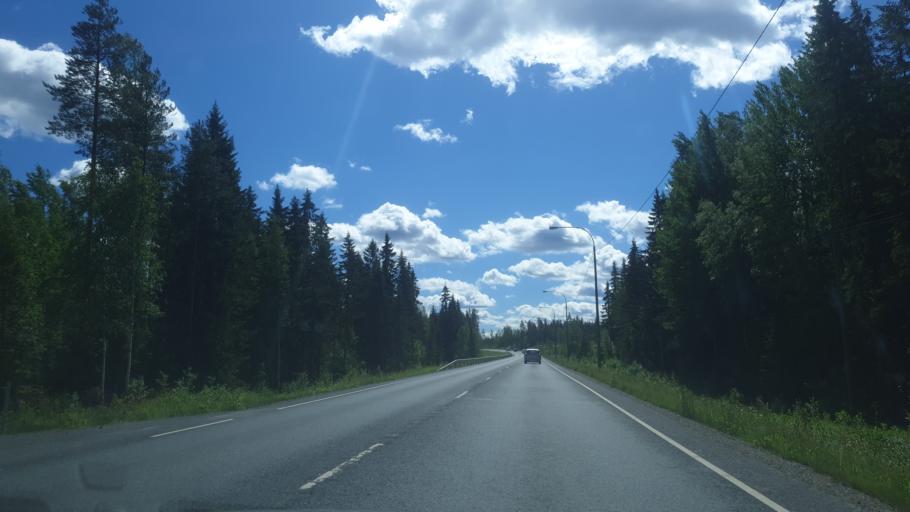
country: FI
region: Northern Savo
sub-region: Varkaus
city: Leppaevirta
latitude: 62.5725
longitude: 27.6089
